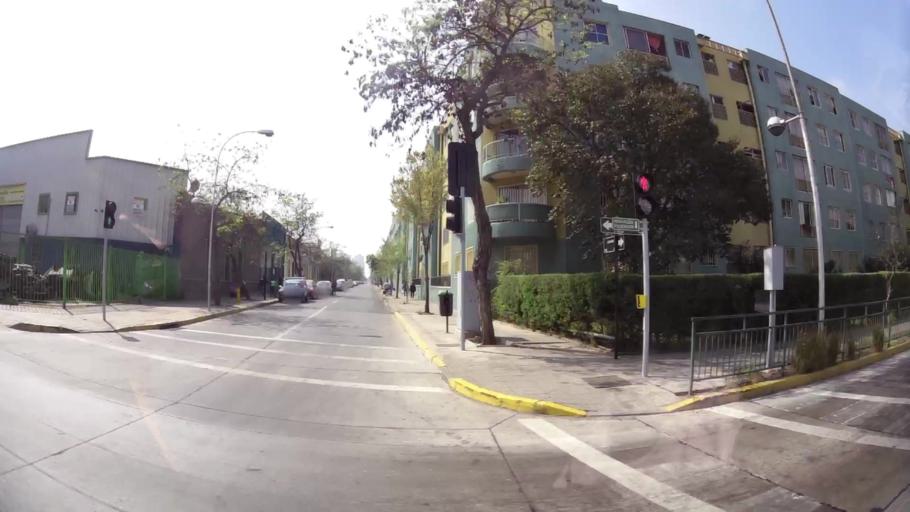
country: CL
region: Santiago Metropolitan
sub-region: Provincia de Santiago
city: Santiago
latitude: -33.4557
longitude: -70.6435
